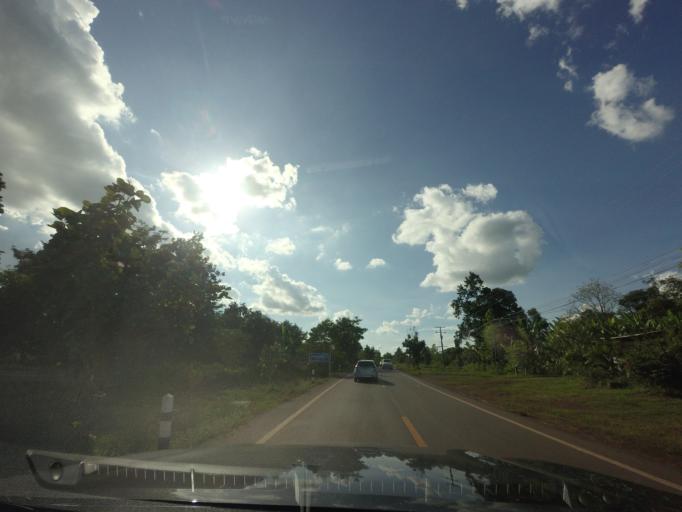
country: TH
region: Changwat Udon Thani
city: Ban Dung
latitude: 17.7430
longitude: 103.3092
